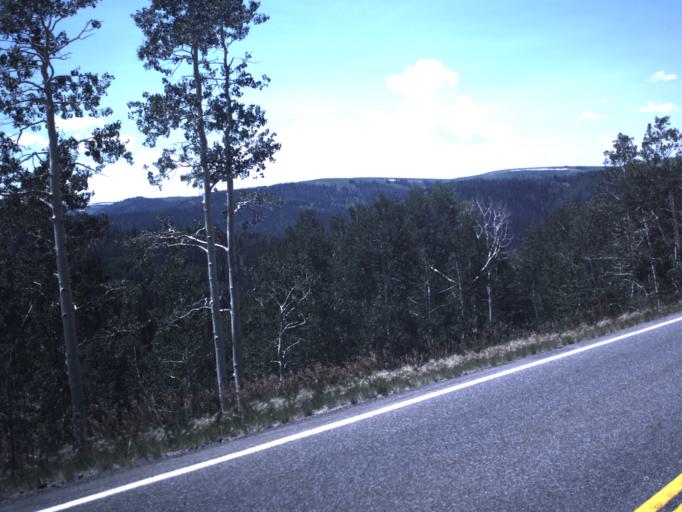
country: US
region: Utah
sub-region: Sanpete County
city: Fairview
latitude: 39.6806
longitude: -111.2249
